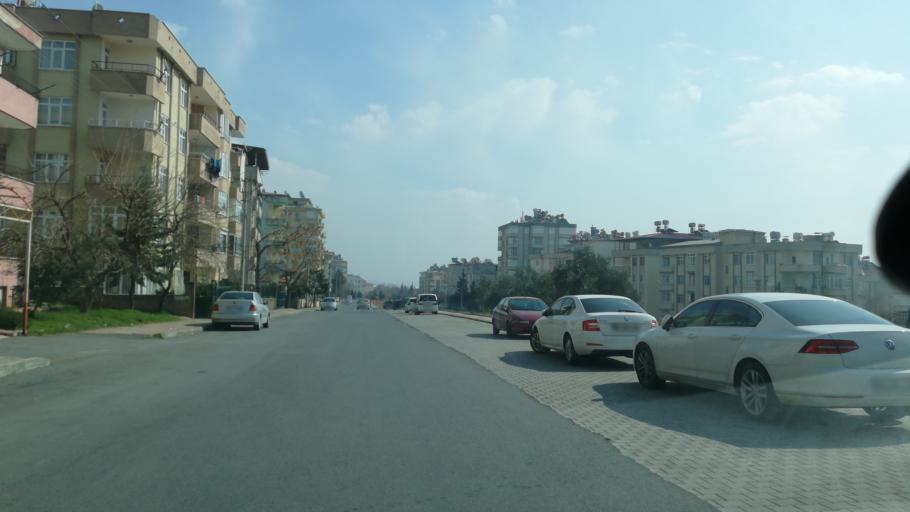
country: TR
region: Kahramanmaras
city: Kahramanmaras
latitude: 37.5890
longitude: 36.8952
